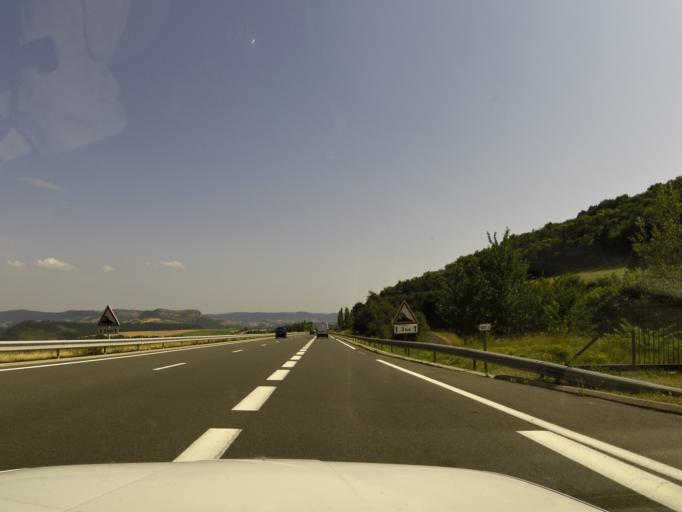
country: FR
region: Languedoc-Roussillon
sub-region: Departement de la Lozere
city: Marvejols
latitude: 44.5608
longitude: 3.2539
